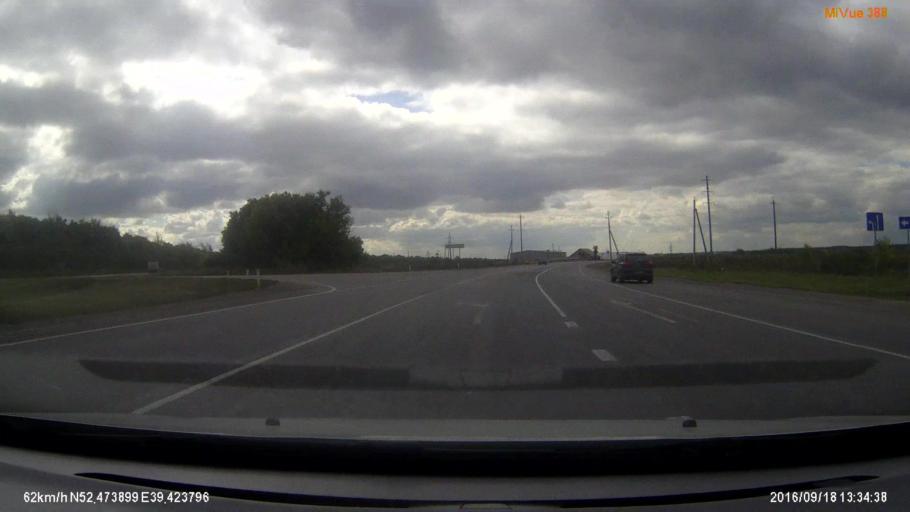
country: RU
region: Lipetsk
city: Borinskoye
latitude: 52.4518
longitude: 39.3730
